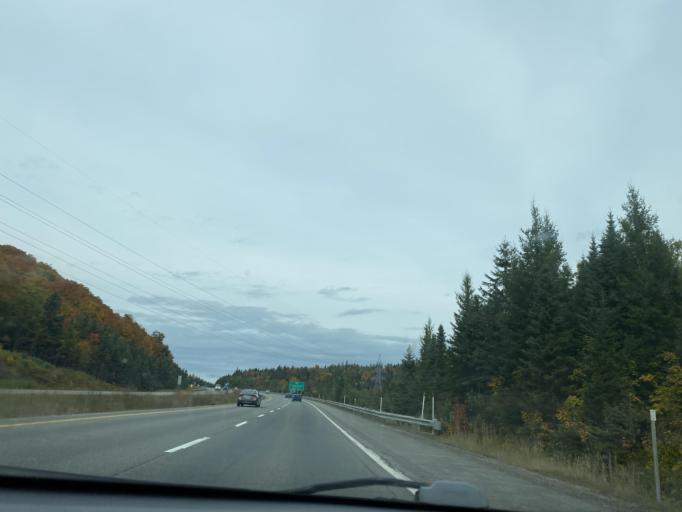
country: CA
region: Quebec
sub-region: Laurentides
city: Sainte-Agathe-des-Monts
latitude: 46.0293
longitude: -74.2634
